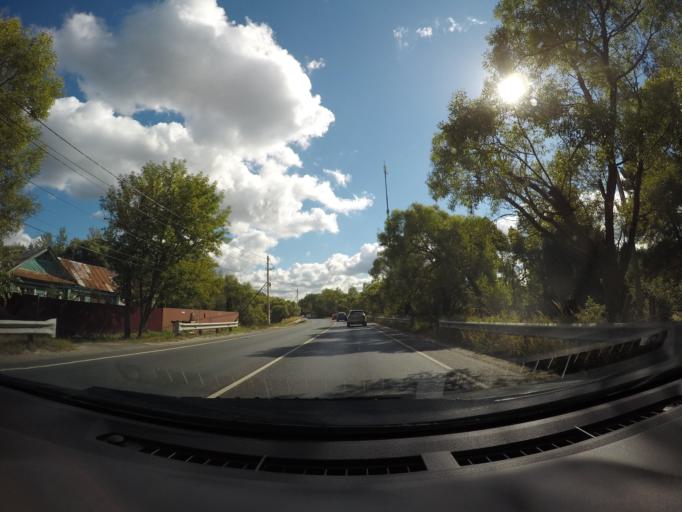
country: RU
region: Moskovskaya
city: Gzhel'
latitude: 55.6355
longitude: 38.3249
